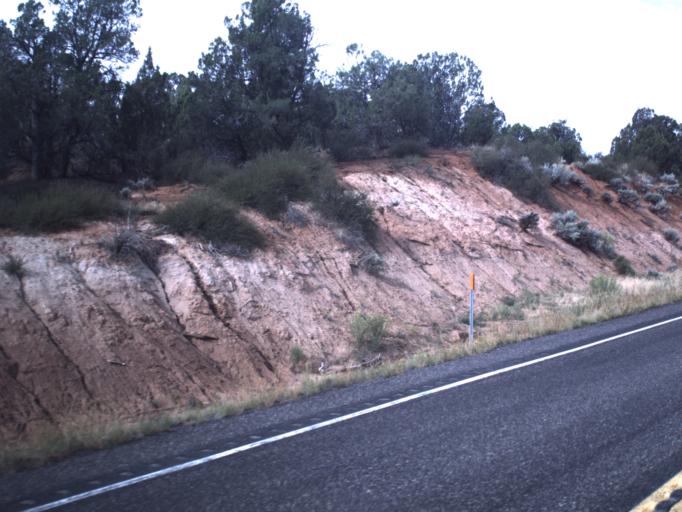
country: US
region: Utah
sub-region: Kane County
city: Kanab
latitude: 37.2205
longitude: -112.7082
